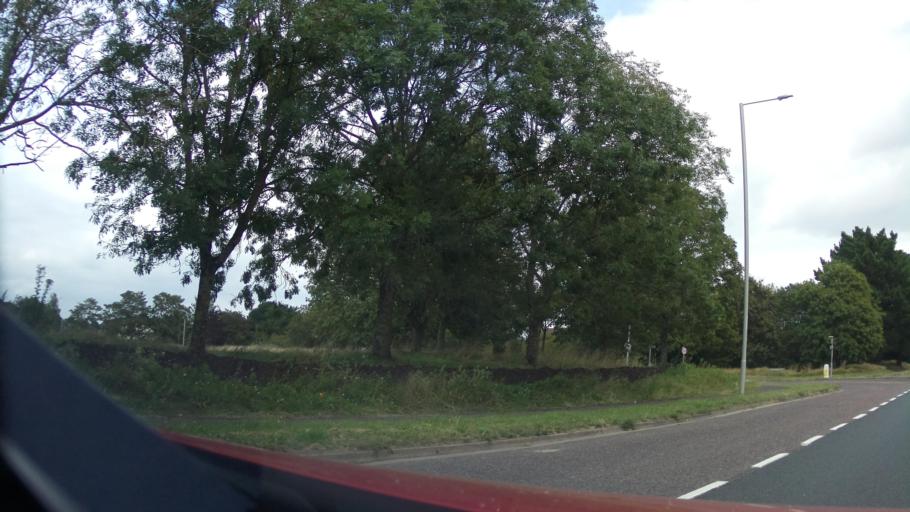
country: GB
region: England
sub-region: Hampshire
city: Bransgore
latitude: 50.7421
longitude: -1.7371
